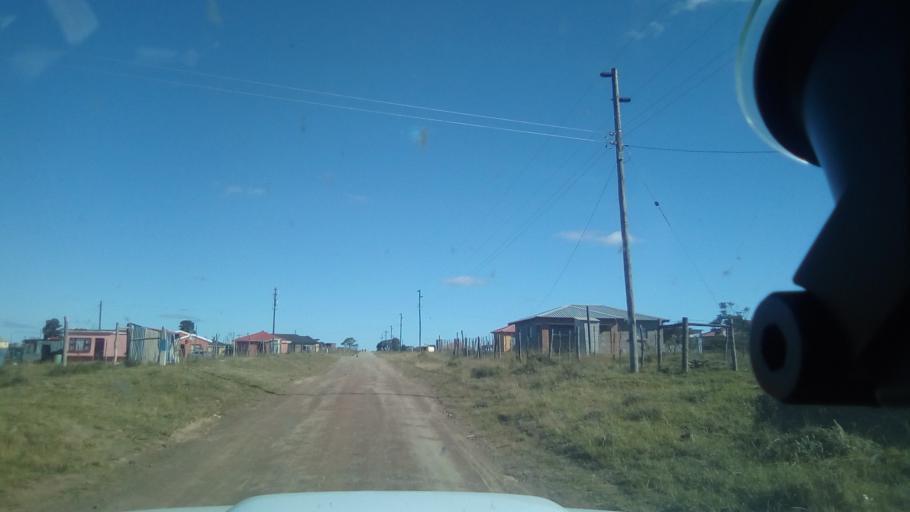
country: ZA
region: Eastern Cape
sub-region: Buffalo City Metropolitan Municipality
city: Bhisho
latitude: -32.7869
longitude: 27.3273
